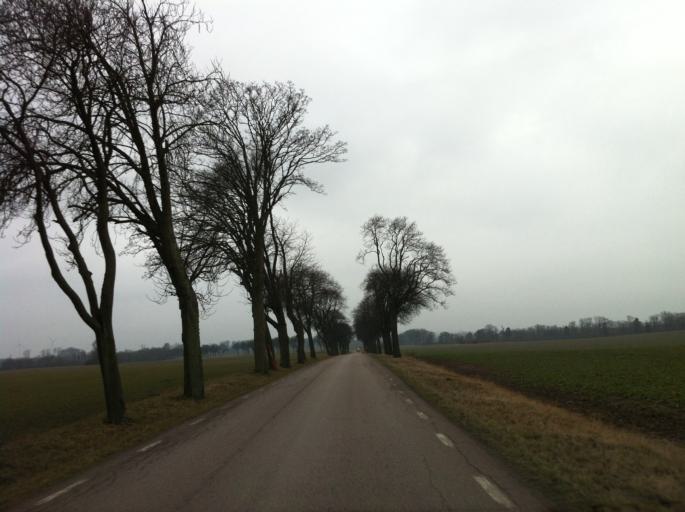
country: SE
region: Skane
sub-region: Svalovs Kommun
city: Kagerod
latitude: 55.9698
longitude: 13.0858
